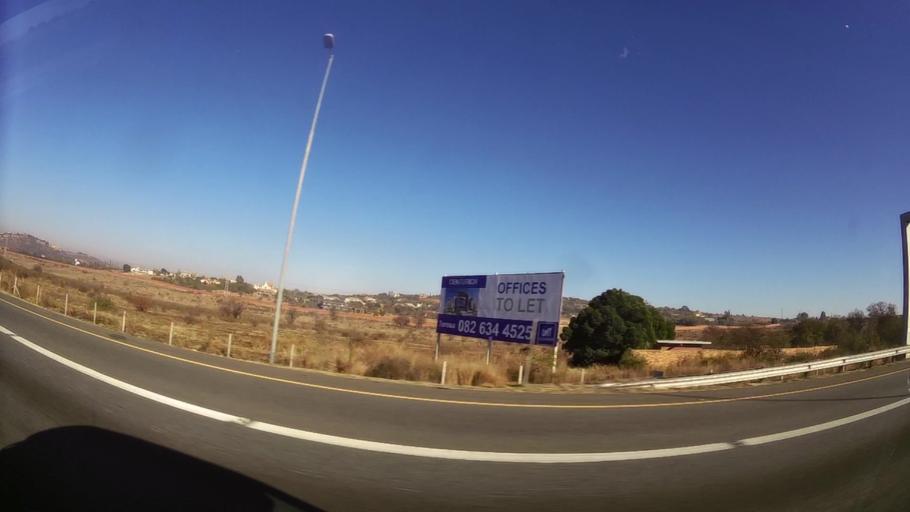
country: ZA
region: Gauteng
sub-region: City of Tshwane Metropolitan Municipality
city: Centurion
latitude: -25.8708
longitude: 28.2541
